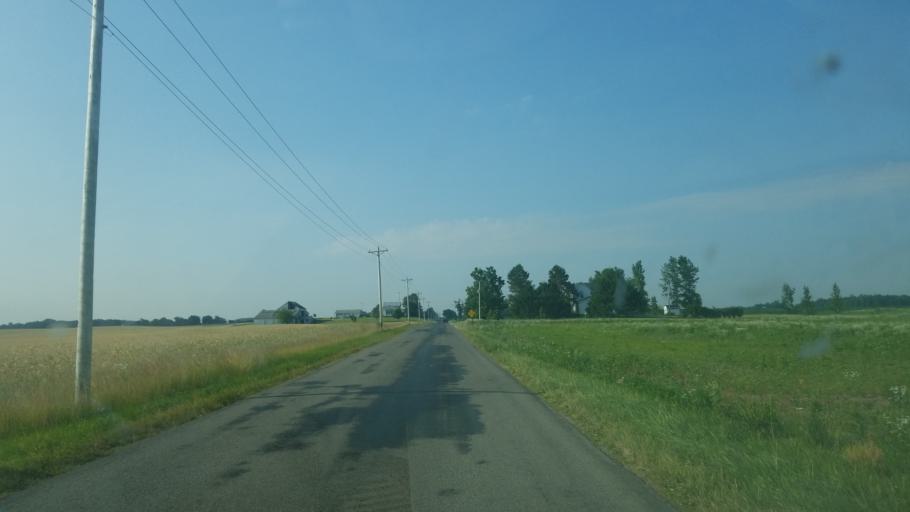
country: US
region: Ohio
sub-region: Hardin County
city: Kenton
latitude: 40.6193
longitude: -83.7199
